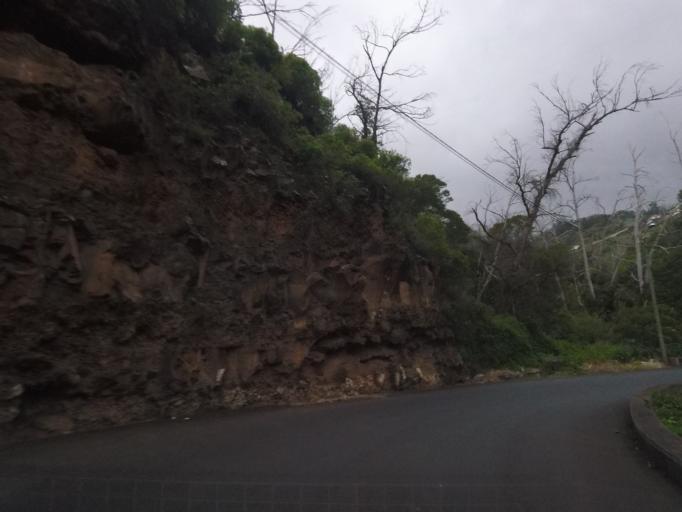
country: PT
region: Madeira
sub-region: Machico
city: Machico
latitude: 32.7039
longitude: -16.7725
